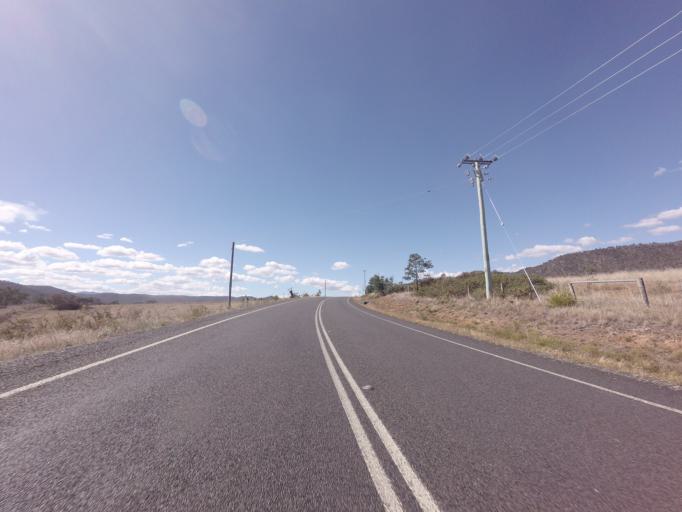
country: AU
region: Tasmania
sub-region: Break O'Day
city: St Helens
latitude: -41.7133
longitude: 147.8378
